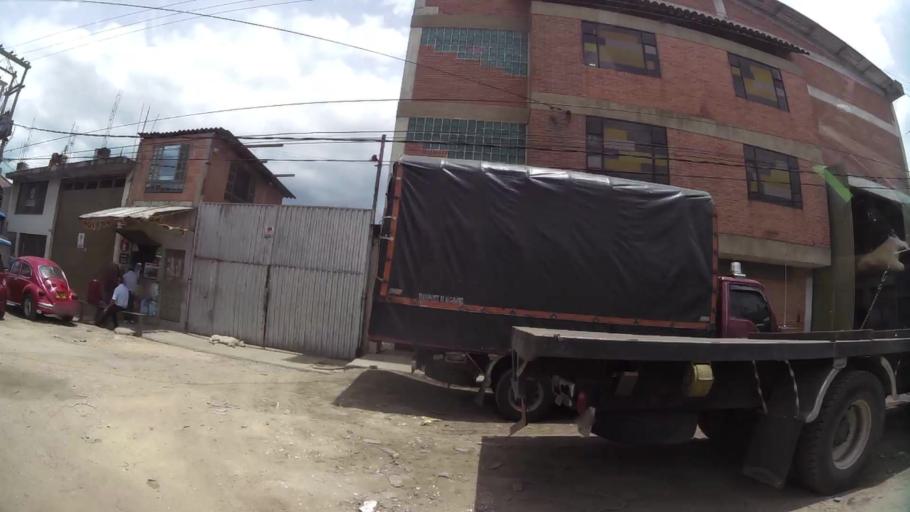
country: CO
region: Bogota D.C.
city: Bogota
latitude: 4.6474
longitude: -74.1473
